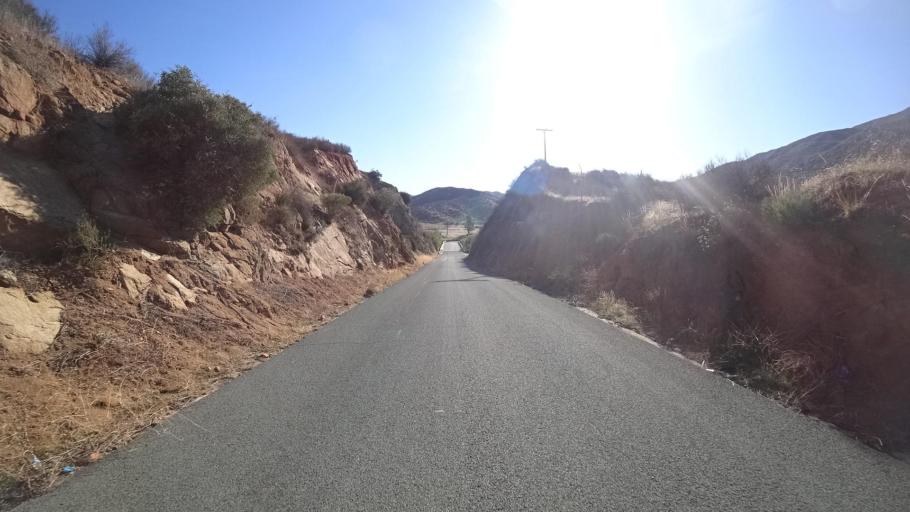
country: MX
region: Baja California
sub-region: Tecate
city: Lomas de Santa Anita
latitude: 32.6108
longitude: -116.7009
